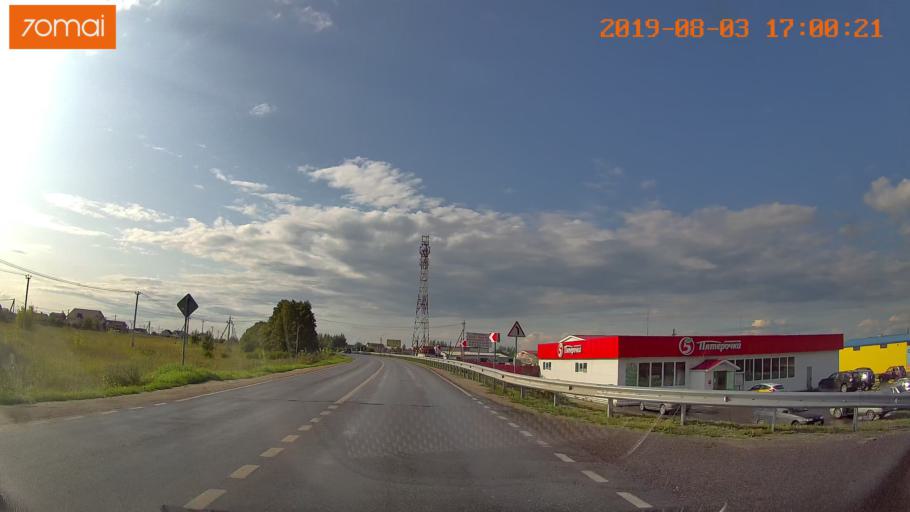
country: RU
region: Moskovskaya
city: Voskresensk
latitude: 55.3365
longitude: 38.6184
